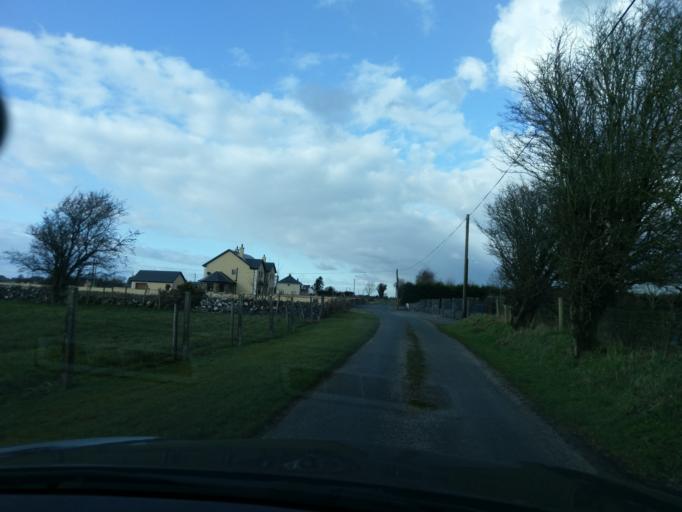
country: IE
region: Connaught
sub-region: County Galway
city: Athenry
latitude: 53.4544
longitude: -8.6431
